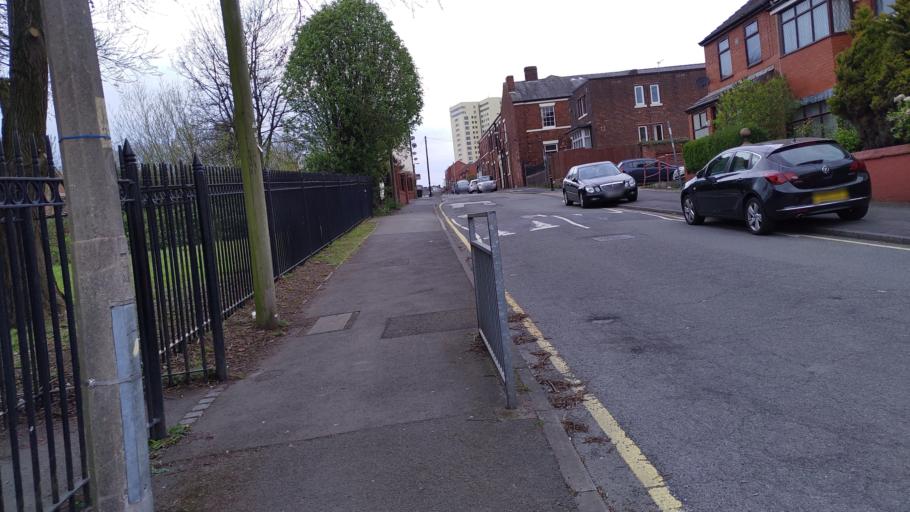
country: GB
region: England
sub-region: Lancashire
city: Preston
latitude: 53.7538
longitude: -2.6920
